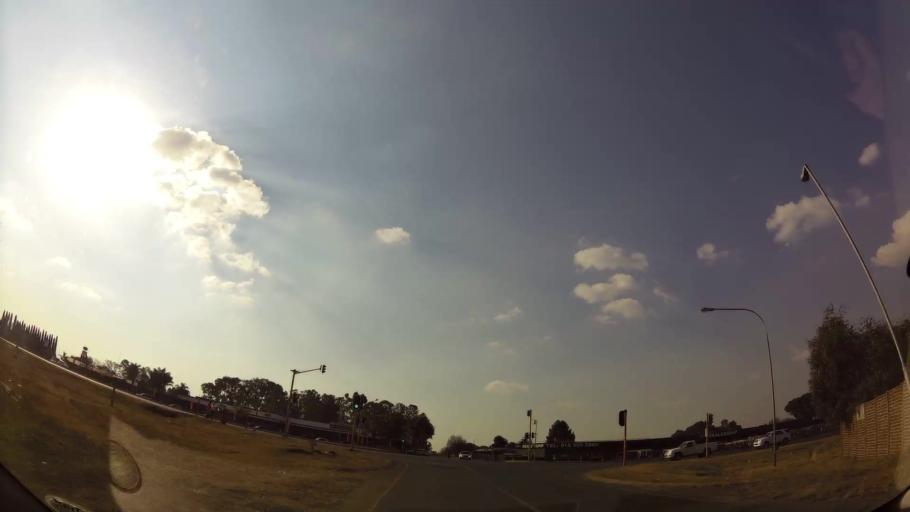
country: ZA
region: Gauteng
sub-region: Ekurhuleni Metropolitan Municipality
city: Benoni
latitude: -26.1177
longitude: 28.2731
